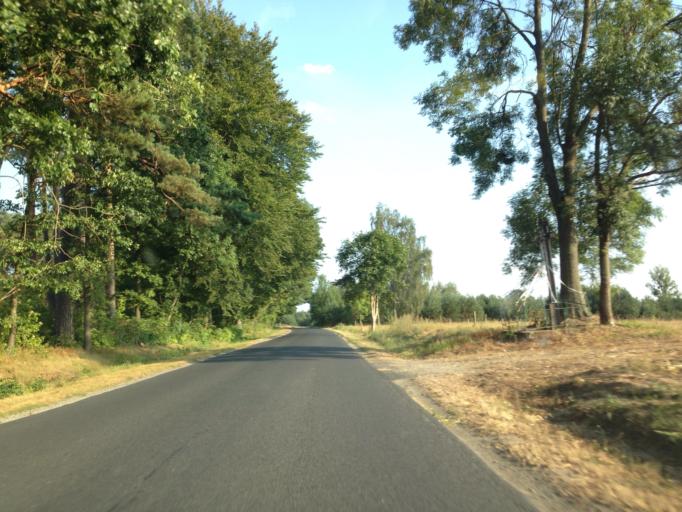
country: PL
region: Warmian-Masurian Voivodeship
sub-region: Powiat nowomiejski
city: Biskupiec
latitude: 53.3889
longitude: 19.3742
